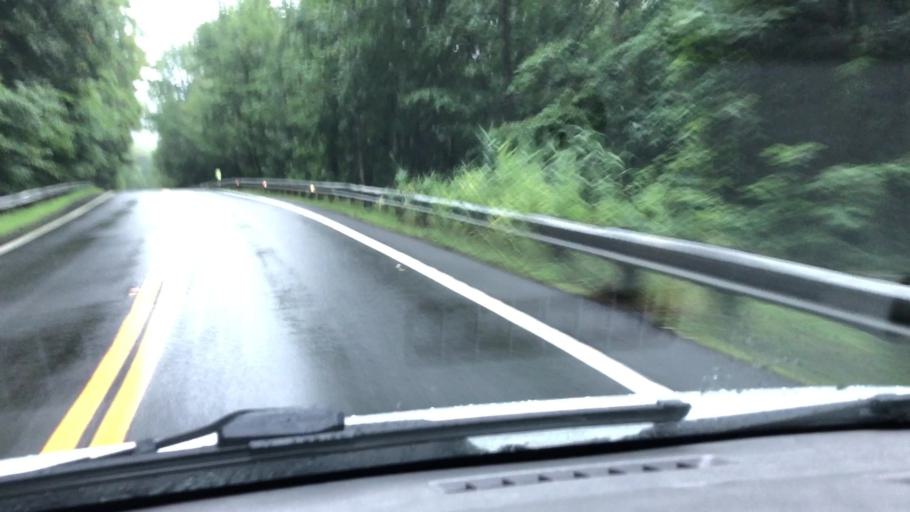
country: US
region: Massachusetts
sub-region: Hampshire County
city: Chesterfield
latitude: 42.3142
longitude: -72.8652
